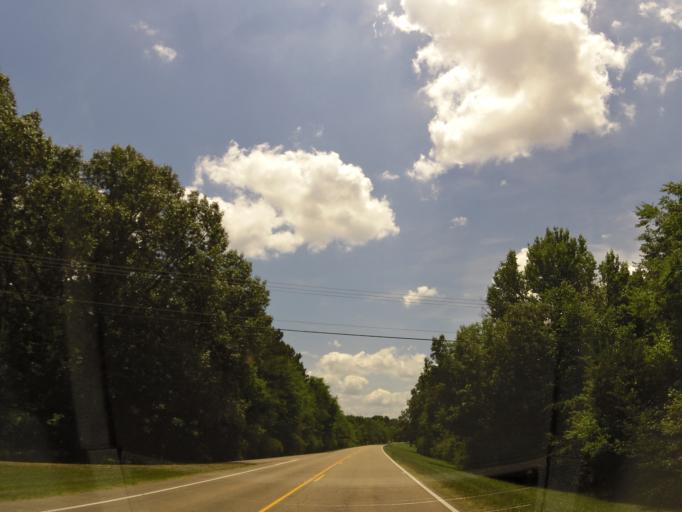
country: US
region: Mississippi
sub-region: Lee County
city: Tupelo
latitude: 34.2505
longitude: -88.7577
